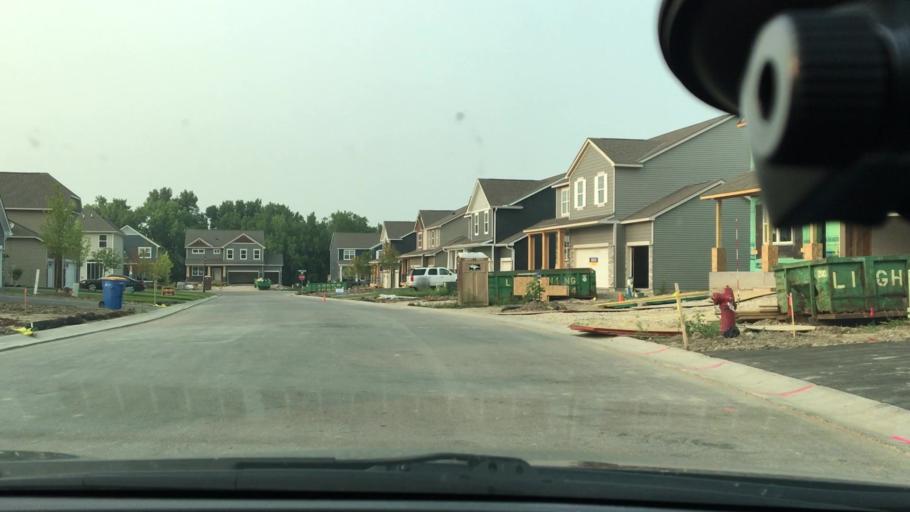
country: US
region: Minnesota
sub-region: Wright County
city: Saint Michael
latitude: 45.2042
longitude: -93.6809
